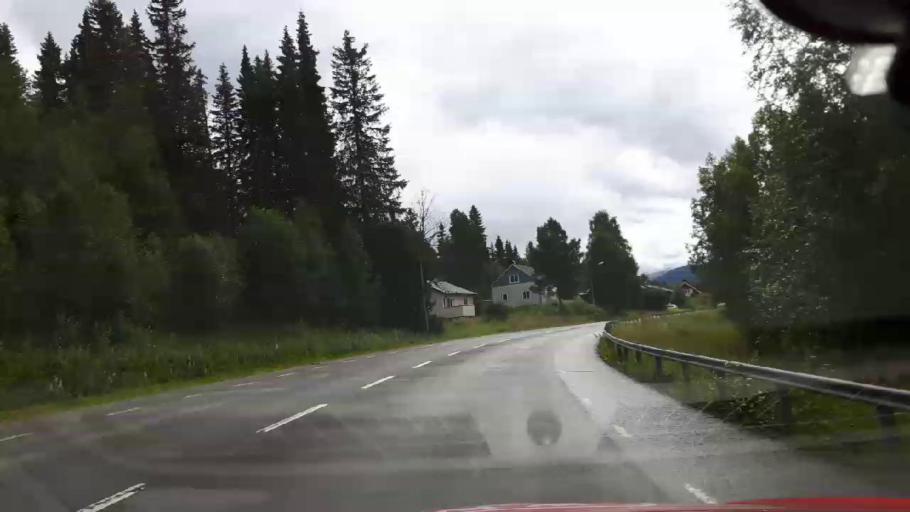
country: NO
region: Nord-Trondelag
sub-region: Lierne
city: Sandvika
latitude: 64.4913
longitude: 14.1514
